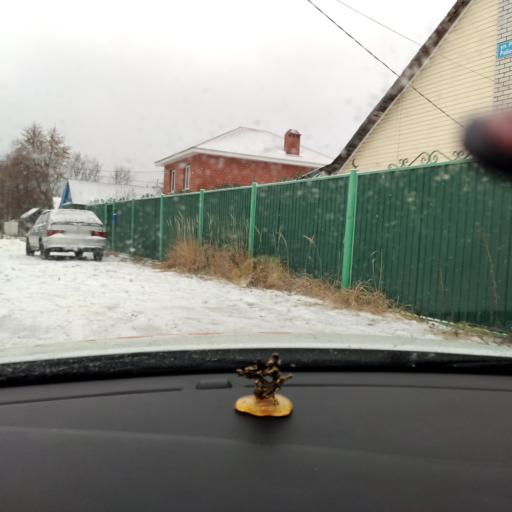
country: RU
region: Tatarstan
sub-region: Gorod Kazan'
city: Kazan
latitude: 55.8749
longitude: 49.1425
